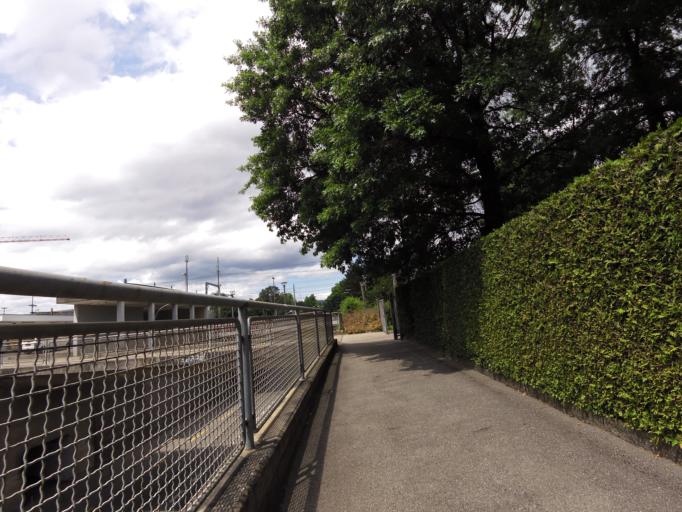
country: CH
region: Bern
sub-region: Oberaargau
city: Langenthal
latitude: 47.2177
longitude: 7.7863
